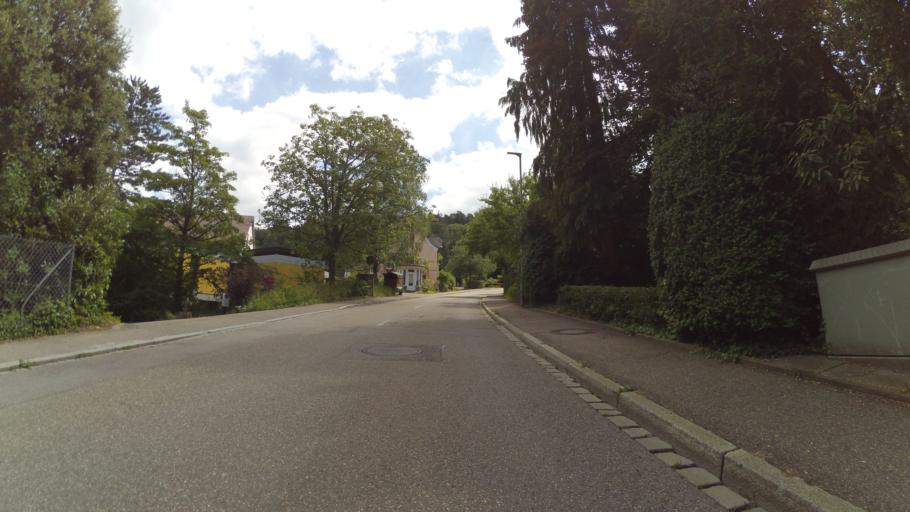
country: DE
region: Baden-Wuerttemberg
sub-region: Freiburg Region
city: Badenweiler
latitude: 47.8010
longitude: 7.6705
